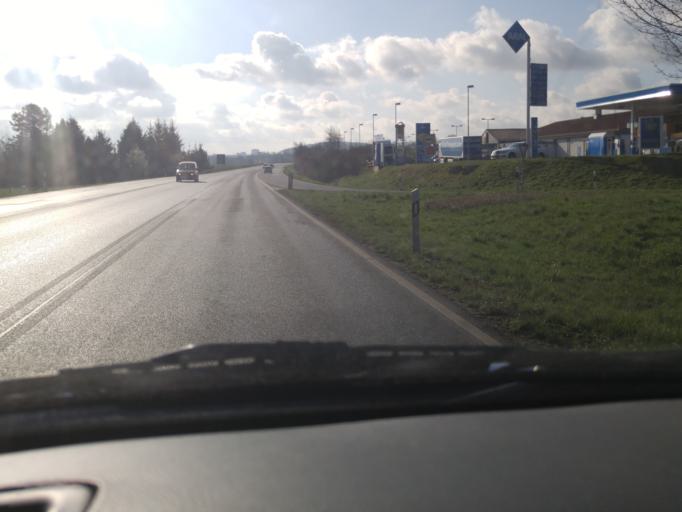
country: DE
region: Hesse
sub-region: Regierungsbezirk Kassel
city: Grossenluder
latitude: 50.5828
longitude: 9.5416
